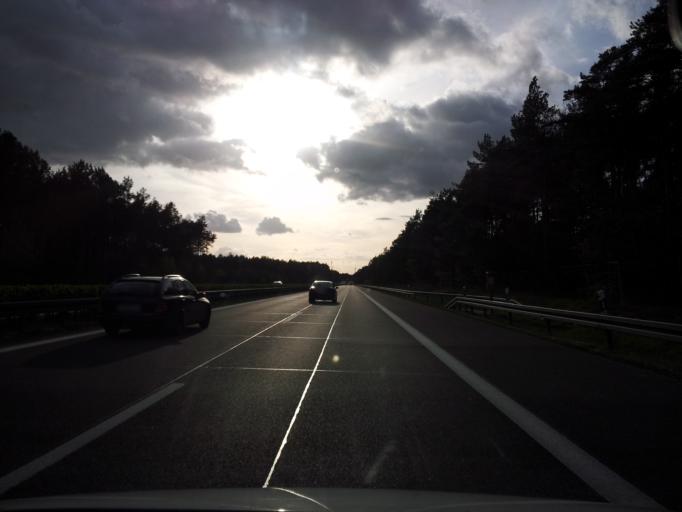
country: DE
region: Brandenburg
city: Kolkwitz
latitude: 51.7270
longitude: 14.2117
